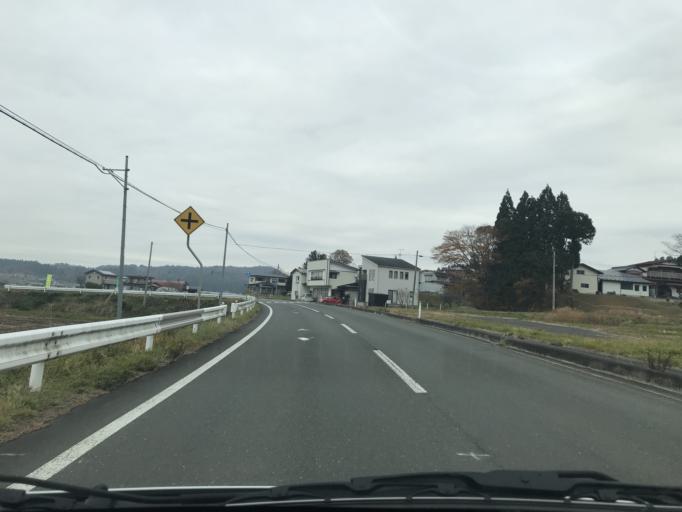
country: JP
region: Iwate
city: Mizusawa
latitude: 39.1695
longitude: 141.2124
